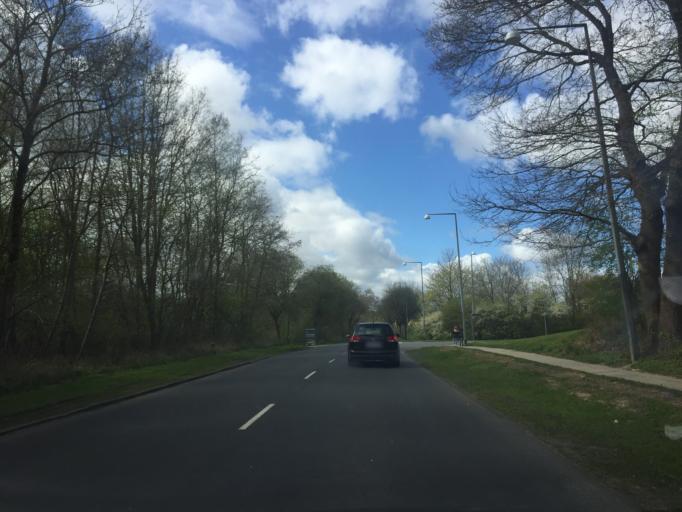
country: DK
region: South Denmark
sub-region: Odense Kommune
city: Bellinge
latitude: 55.3886
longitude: 10.3307
